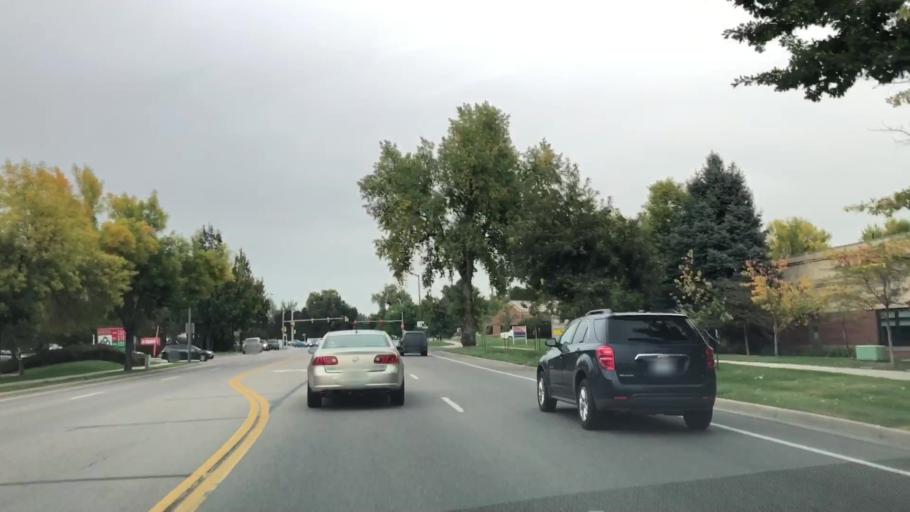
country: US
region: Colorado
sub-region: Larimer County
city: Fort Collins
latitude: 40.5216
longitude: -105.0581
